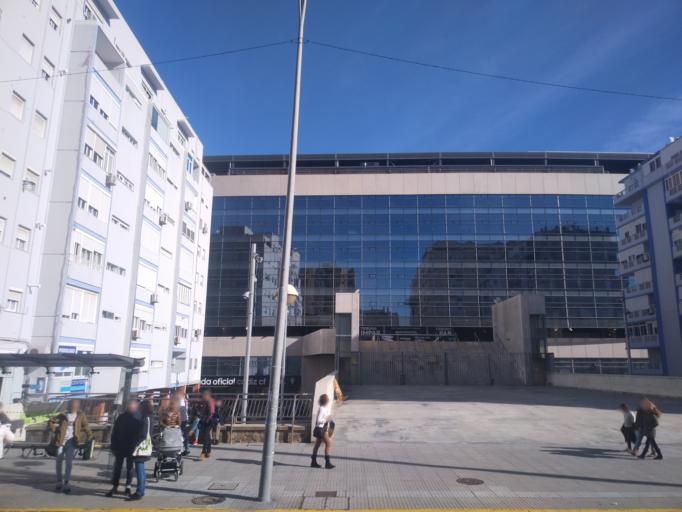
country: ES
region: Andalusia
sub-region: Provincia de Cadiz
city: Cadiz
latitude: 36.5022
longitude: -6.2743
